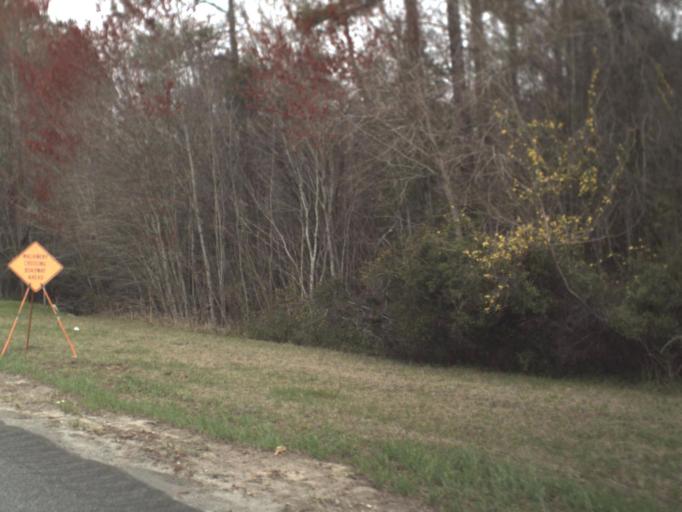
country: US
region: Florida
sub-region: Jefferson County
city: Monticello
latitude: 30.4959
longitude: -83.7421
